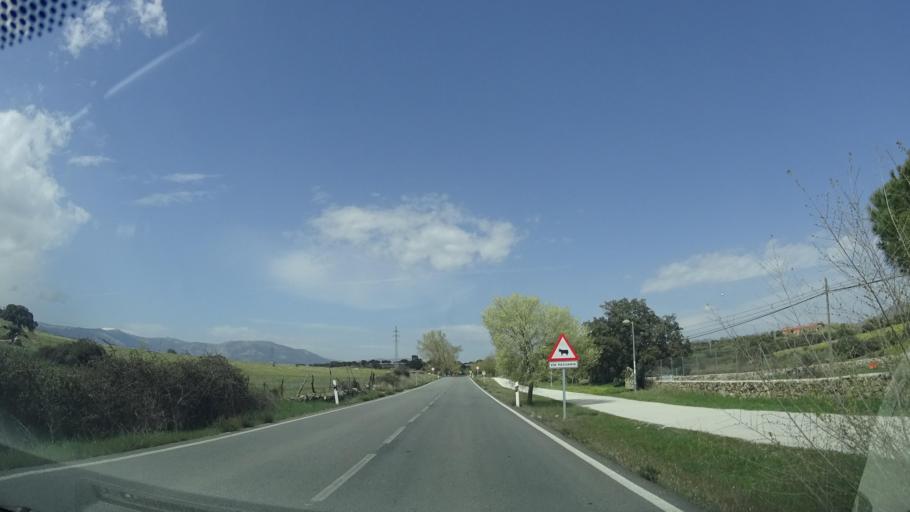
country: ES
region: Madrid
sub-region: Provincia de Madrid
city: Colmenar Viejo
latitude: 40.6886
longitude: -3.7697
